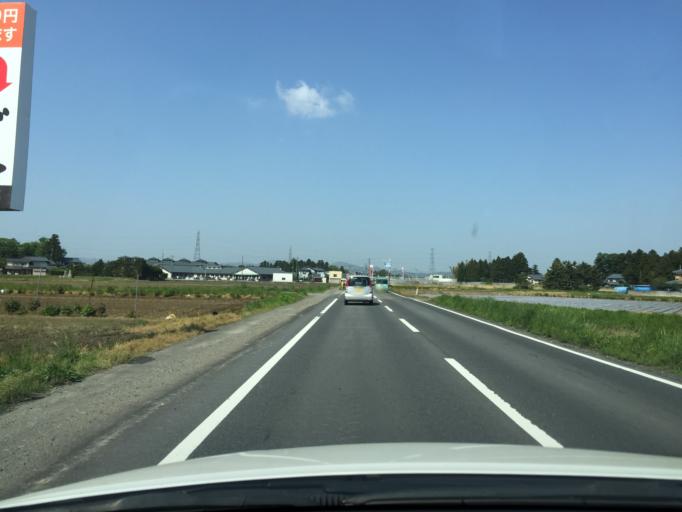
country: JP
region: Niigata
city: Gosen
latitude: 37.7483
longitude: 139.2084
